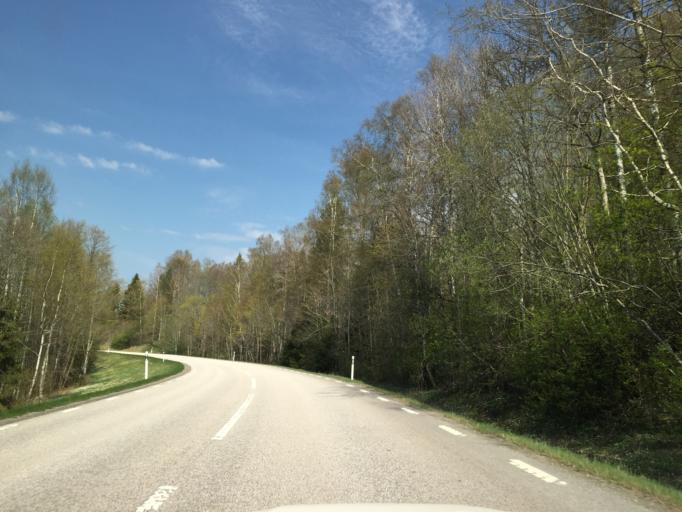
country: SE
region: Vaestra Goetaland
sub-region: Bengtsfors Kommun
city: Dals Langed
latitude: 58.8766
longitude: 12.2143
